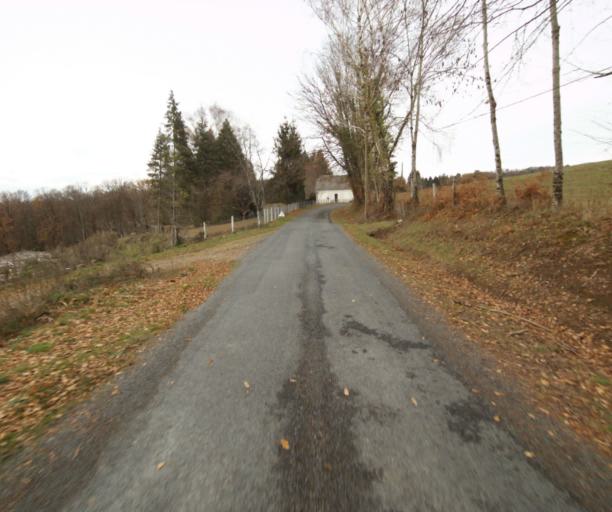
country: FR
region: Limousin
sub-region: Departement de la Correze
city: Saint-Mexant
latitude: 45.2537
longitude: 1.6559
